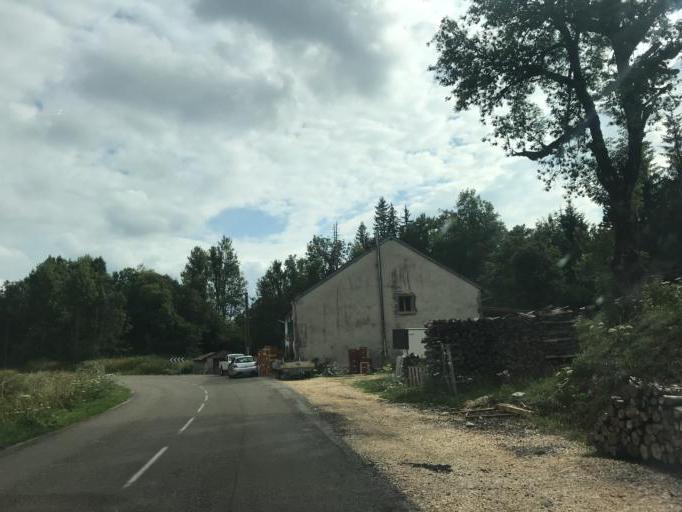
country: FR
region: Franche-Comte
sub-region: Departement du Jura
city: Valfin-les-Saint-Claude
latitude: 46.4737
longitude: 5.8357
